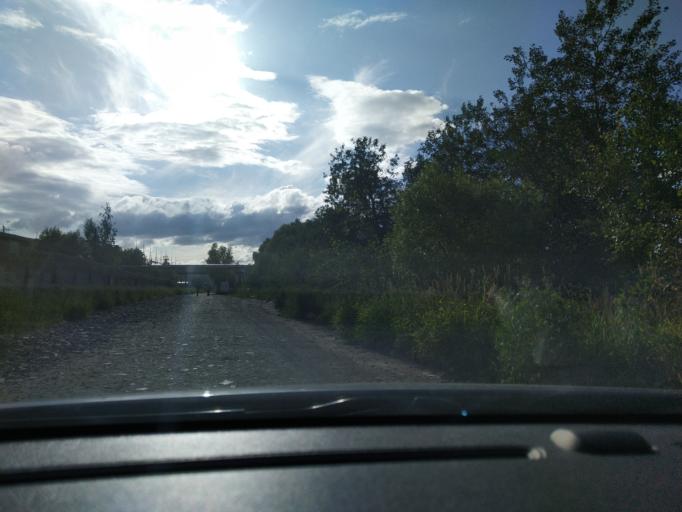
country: RU
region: St.-Petersburg
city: Gorelovo
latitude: 59.7845
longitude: 30.1618
